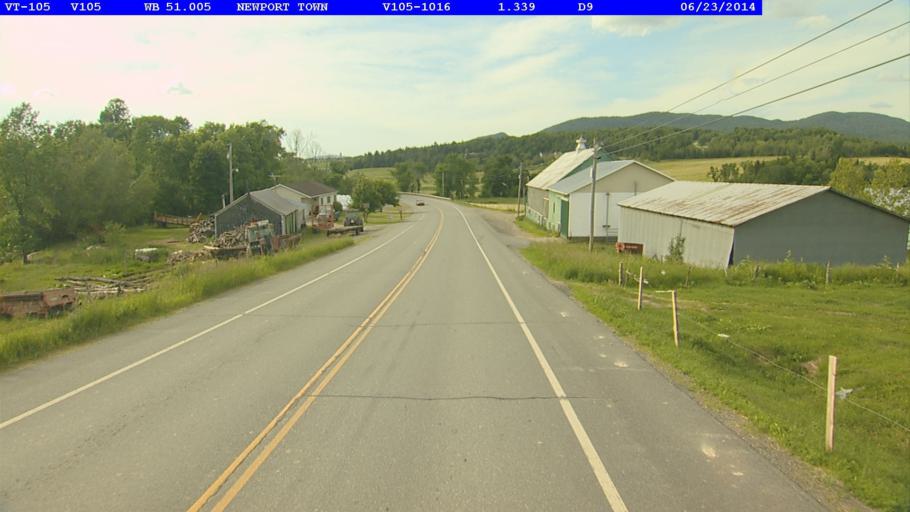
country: US
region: Vermont
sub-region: Orleans County
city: Newport
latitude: 44.9674
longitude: -72.3146
